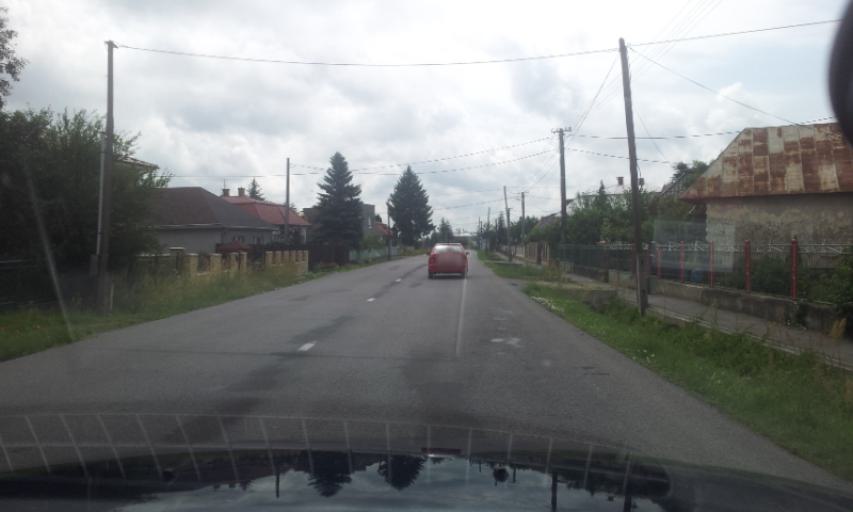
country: SK
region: Kosicky
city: Michalovce
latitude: 48.6904
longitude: 21.9813
